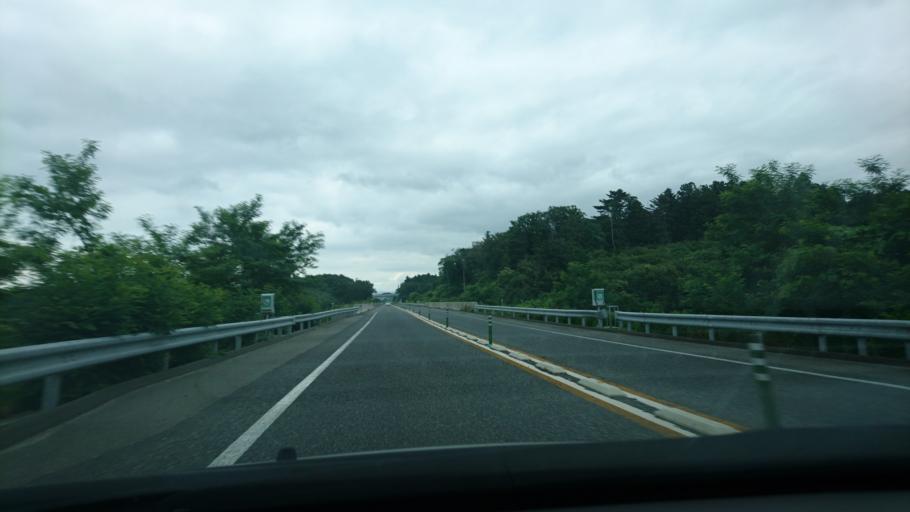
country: JP
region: Iwate
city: Ichinoseki
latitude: 38.7342
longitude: 141.0945
